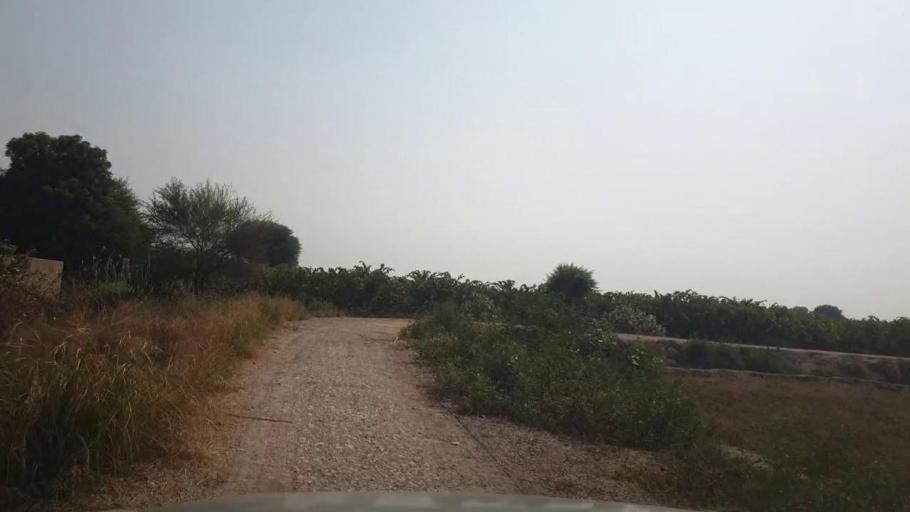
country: PK
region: Sindh
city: Bhit Shah
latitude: 25.7303
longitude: 68.4970
